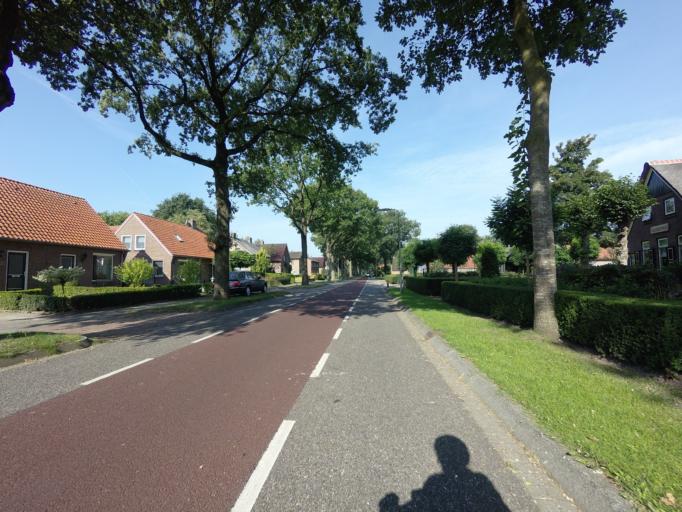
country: NL
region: Overijssel
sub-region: Gemeente Hardenberg
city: Hardenberg
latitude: 52.5666
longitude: 6.6632
